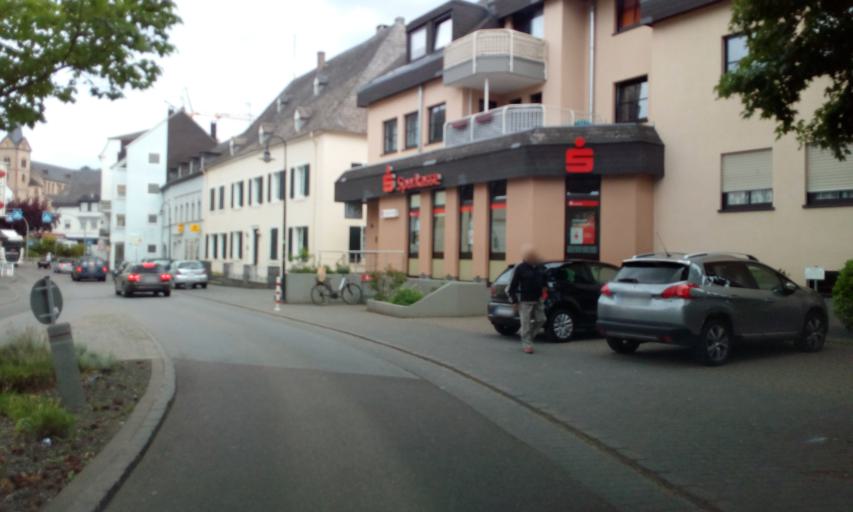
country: DE
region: Rheinland-Pfalz
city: Kenn
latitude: 49.7835
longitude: 6.7090
